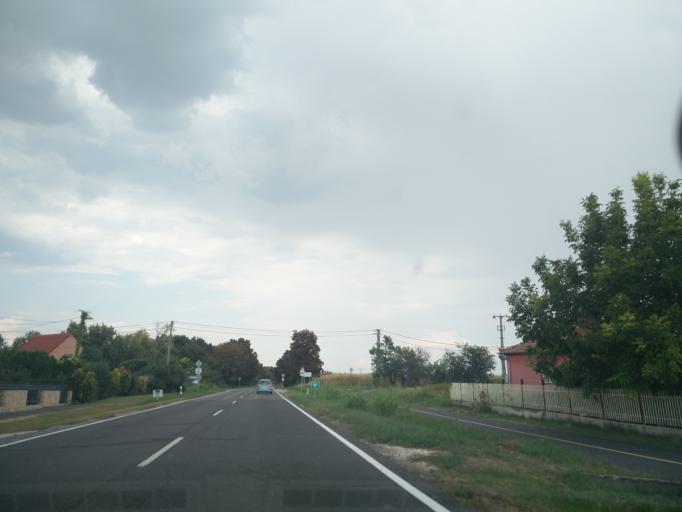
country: HU
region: Fejer
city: Polgardi
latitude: 47.0614
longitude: 18.3082
